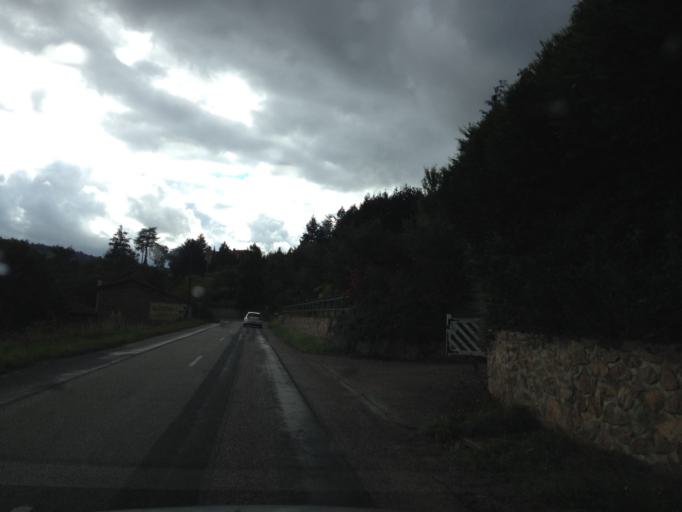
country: FR
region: Rhone-Alpes
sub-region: Departement de la Loire
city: Renaison
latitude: 46.0505
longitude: 3.9109
